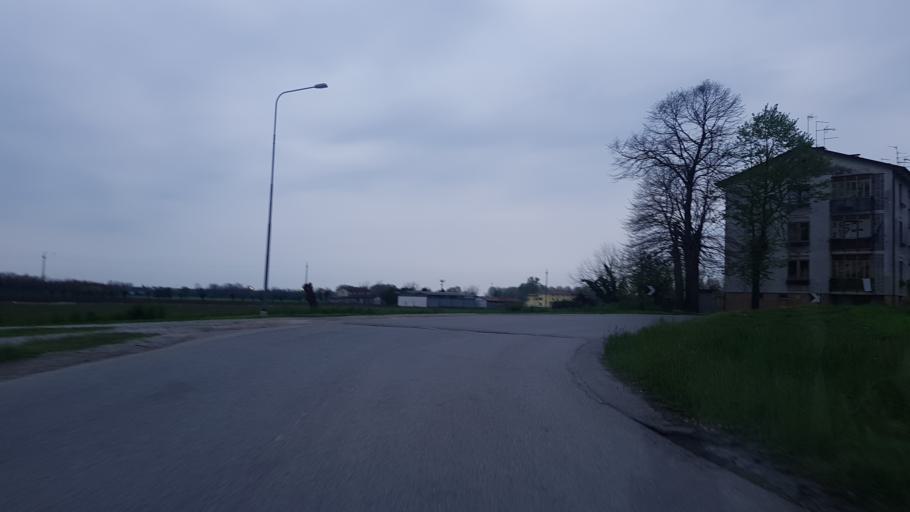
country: IT
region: Friuli Venezia Giulia
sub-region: Provincia di Udine
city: Palmanova
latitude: 45.8980
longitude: 13.3138
